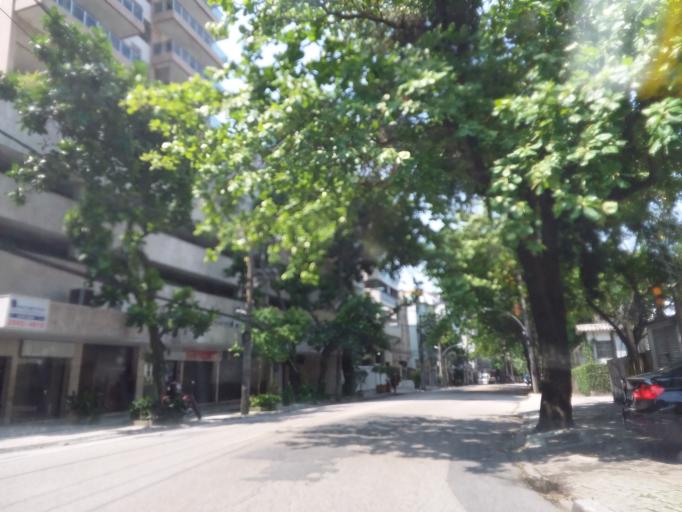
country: BR
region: Rio de Janeiro
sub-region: Rio De Janeiro
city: Rio de Janeiro
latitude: -22.9775
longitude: -43.2326
